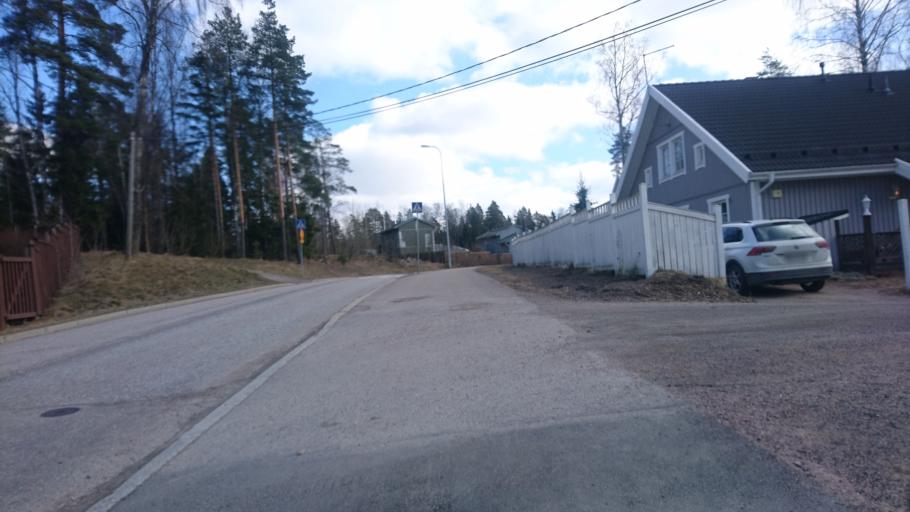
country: FI
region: Uusimaa
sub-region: Helsinki
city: Kauniainen
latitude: 60.1996
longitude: 24.7204
